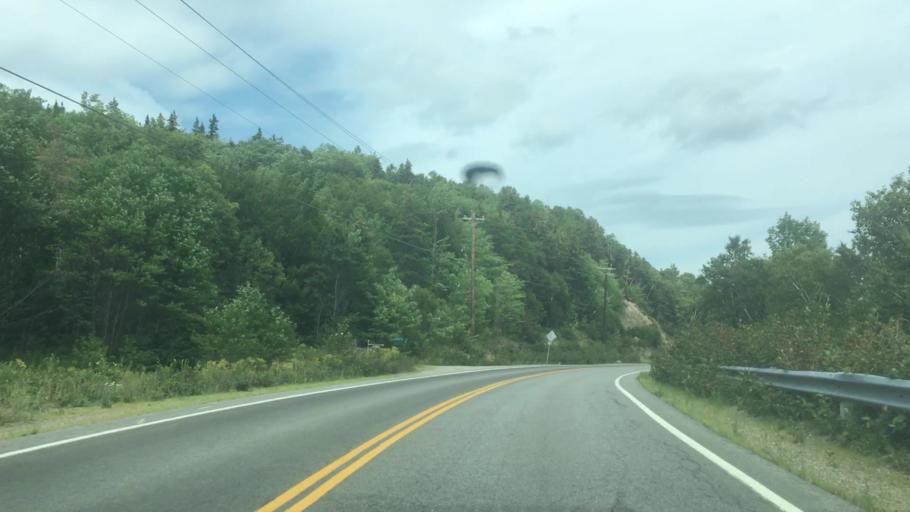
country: CA
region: Nova Scotia
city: Sydney Mines
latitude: 46.5329
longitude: -60.4171
